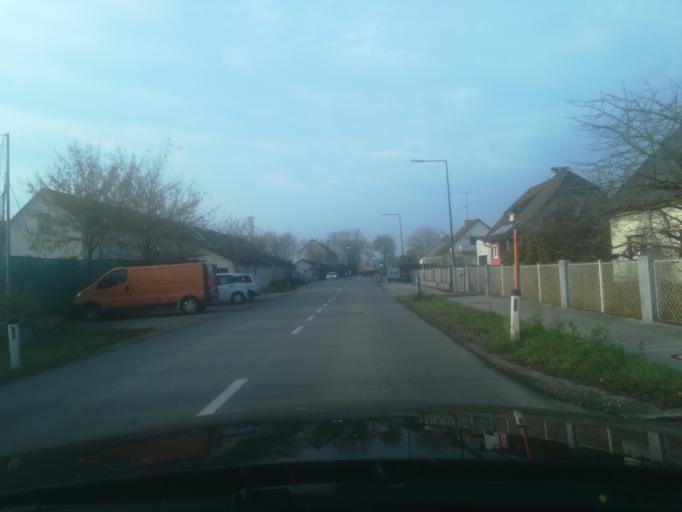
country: AT
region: Upper Austria
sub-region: Wels Stadt
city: Wels
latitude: 48.1680
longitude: 13.9988
